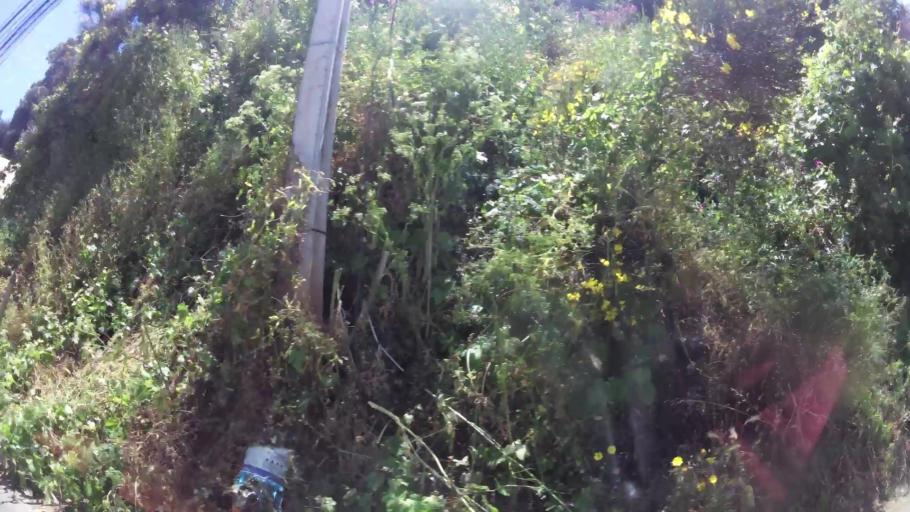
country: CL
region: Valparaiso
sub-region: Provincia de Valparaiso
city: Valparaiso
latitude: -33.0522
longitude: -71.6330
